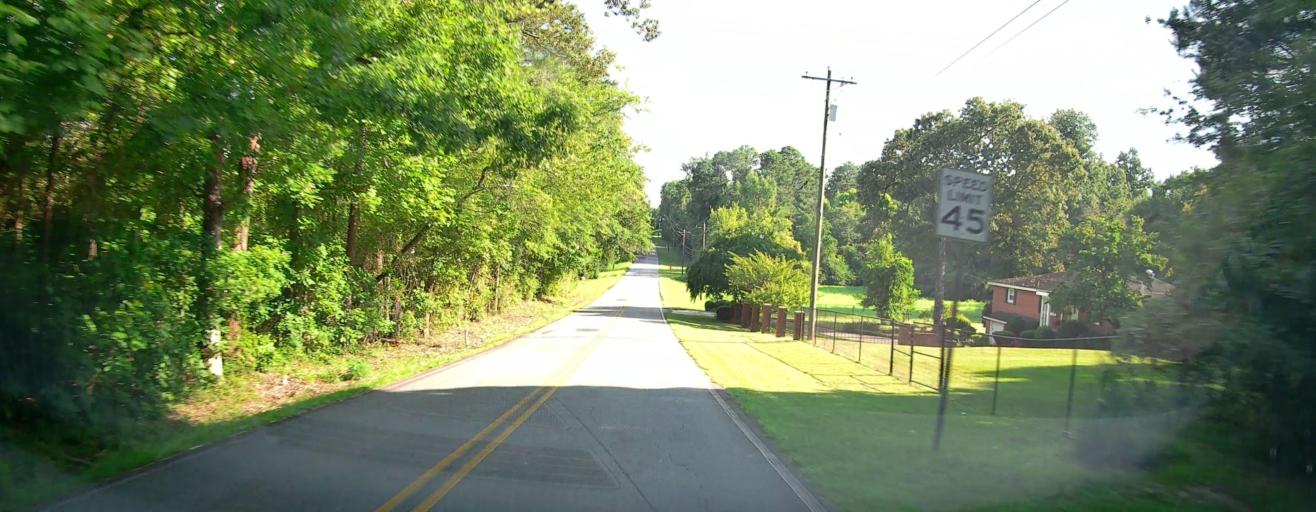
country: US
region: Georgia
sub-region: Houston County
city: Centerville
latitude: 32.6120
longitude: -83.6610
